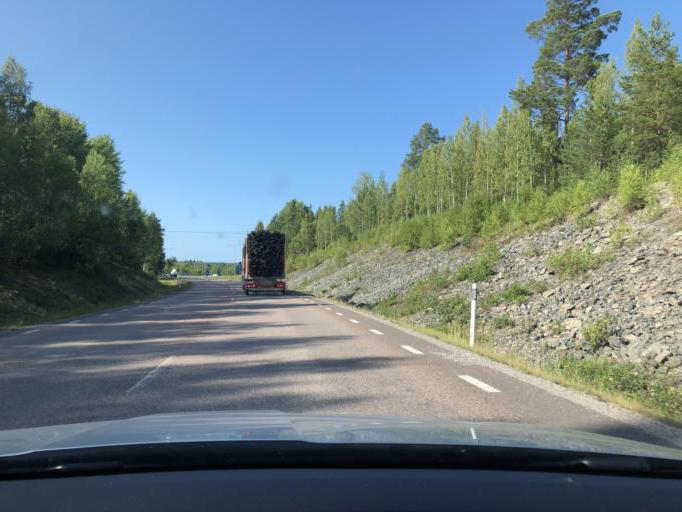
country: SE
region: Dalarna
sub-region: Faluns Kommun
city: Falun
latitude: 60.5835
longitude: 15.7730
